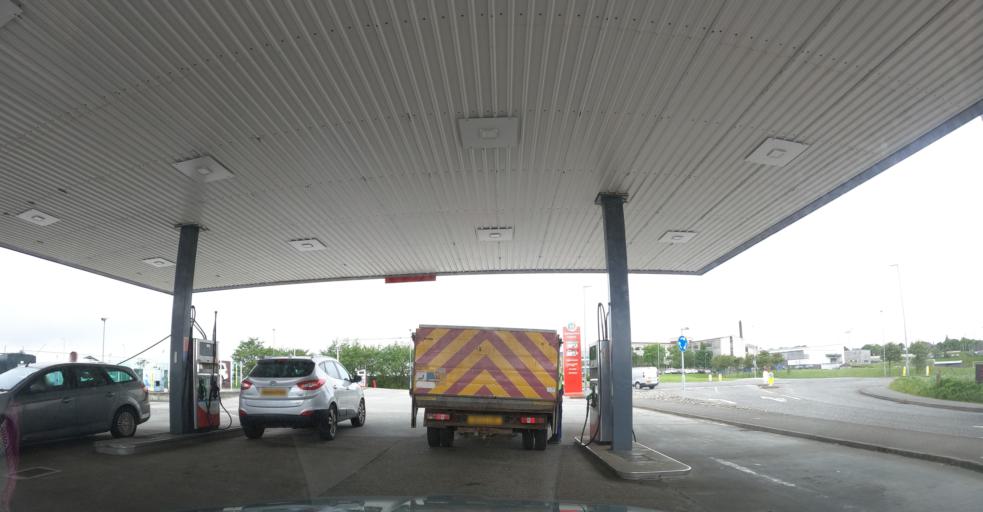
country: GB
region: Scotland
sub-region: Eilean Siar
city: Stornoway
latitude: 58.2085
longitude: -6.3762
